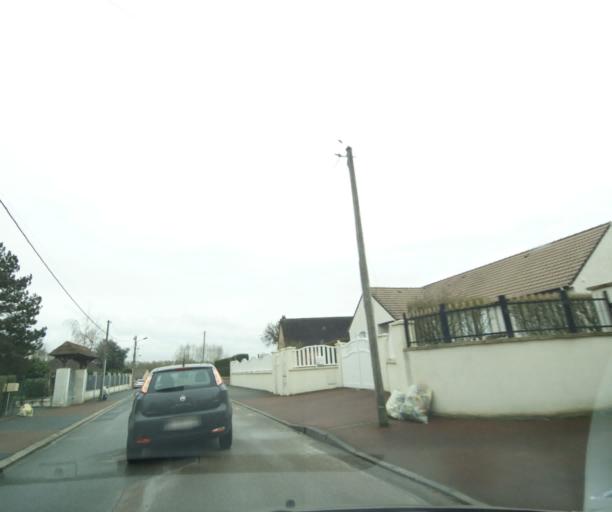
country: FR
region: Picardie
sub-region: Departement de l'Oise
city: Noyon
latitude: 49.5702
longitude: 3.0269
